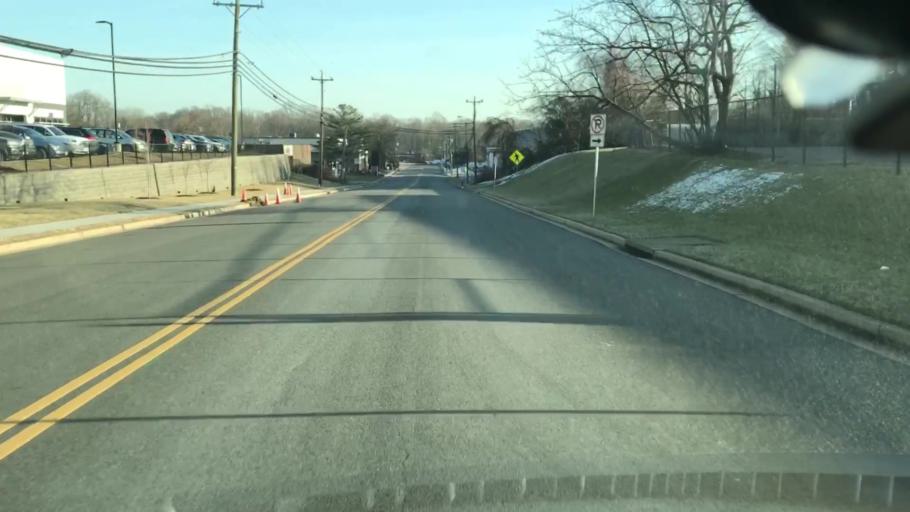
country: US
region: Virginia
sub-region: Fairfax County
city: Ravensworth
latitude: 38.8060
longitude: -77.2162
